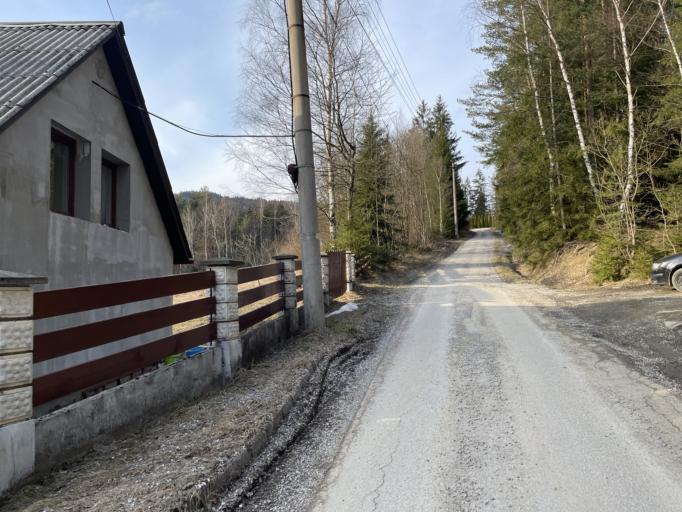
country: CZ
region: Moravskoslezsky
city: Mosty u Jablunkova
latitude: 49.4823
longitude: 18.6945
